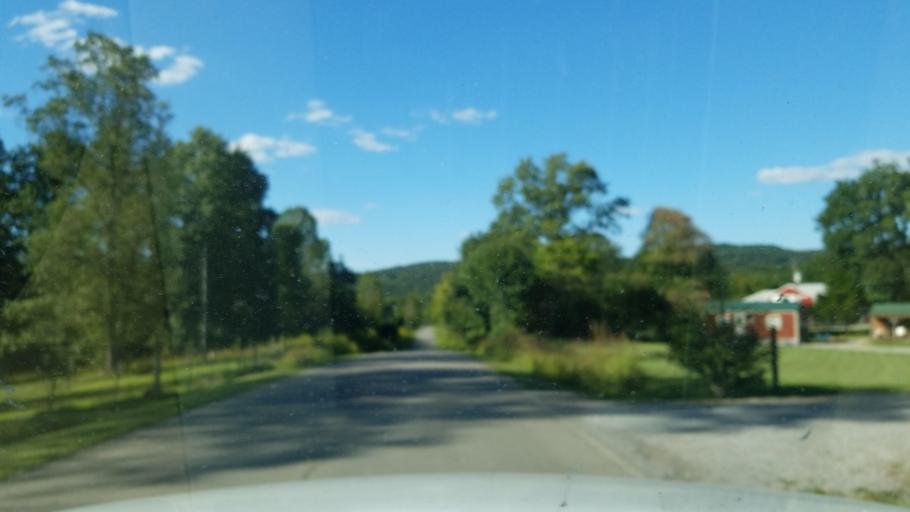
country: US
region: Illinois
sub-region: Hardin County
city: Elizabethtown
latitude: 37.5842
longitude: -88.3654
